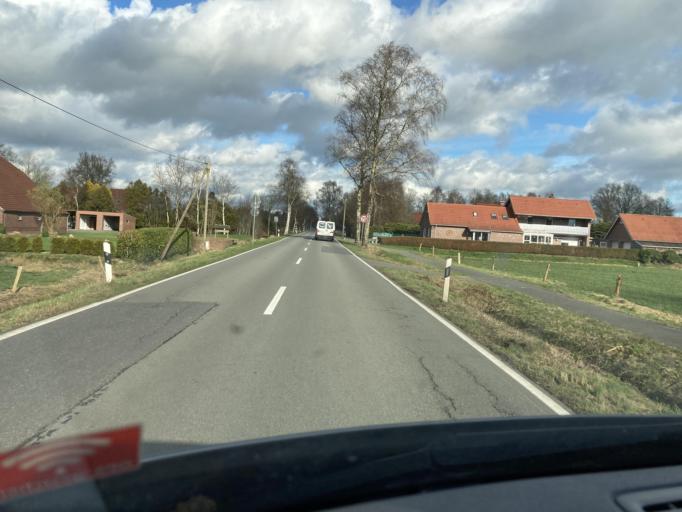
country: DE
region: Lower Saxony
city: Friedeburg
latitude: 53.3720
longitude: 7.8217
